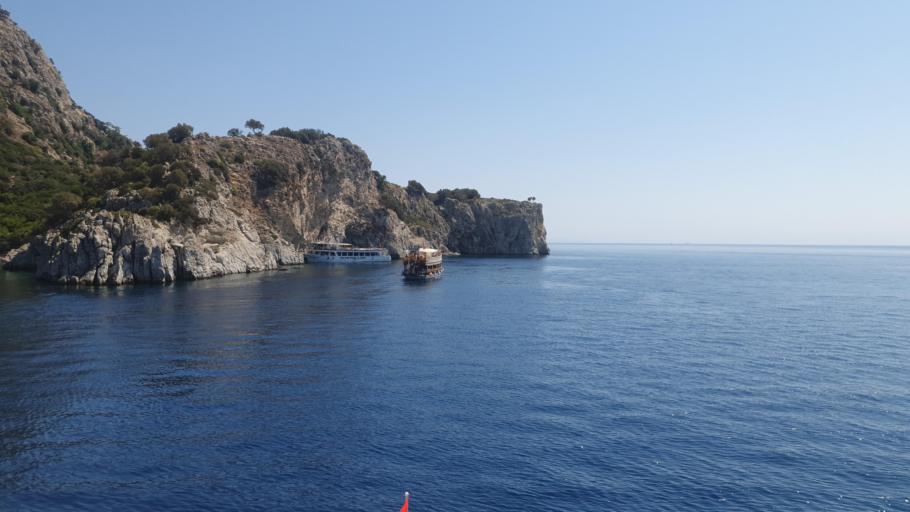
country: TR
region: Mugla
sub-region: Marmaris
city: Marmaris
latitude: 36.7922
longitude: 28.2818
